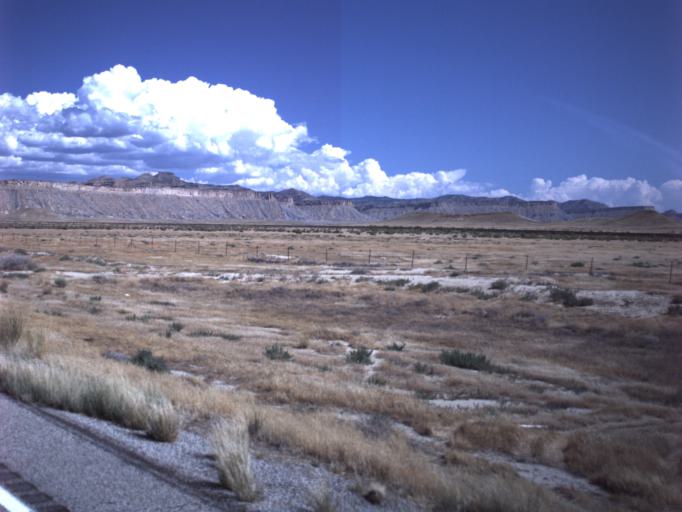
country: US
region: Utah
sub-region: Grand County
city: Moab
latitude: 38.9197
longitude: -109.8152
